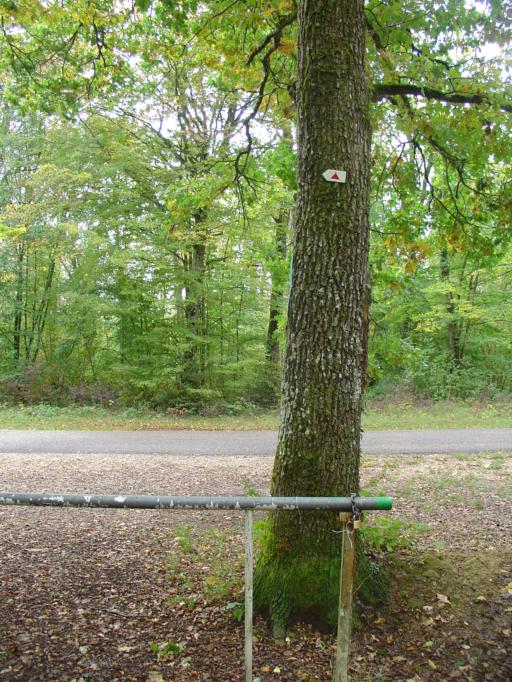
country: FR
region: Lorraine
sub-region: Departement de Meurthe-et-Moselle
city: Colombey-les-Belles
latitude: 48.5922
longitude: 5.9275
